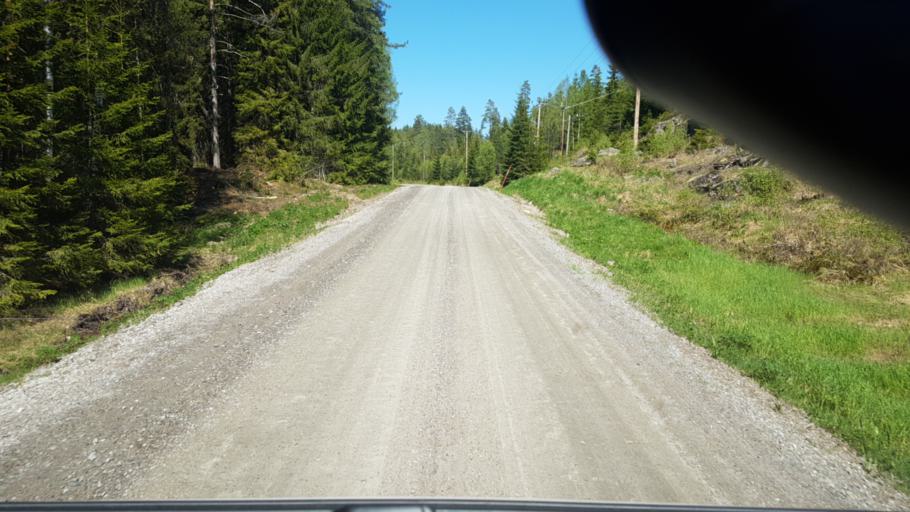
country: SE
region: Vaermland
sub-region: Arvika Kommun
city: Arvika
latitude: 59.8592
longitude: 12.7145
